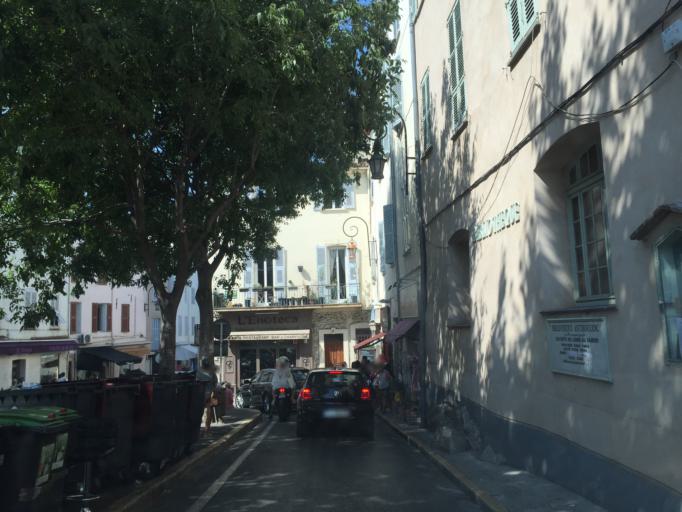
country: FR
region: Provence-Alpes-Cote d'Azur
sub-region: Departement des Alpes-Maritimes
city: Antibes
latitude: 43.5816
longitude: 7.1277
